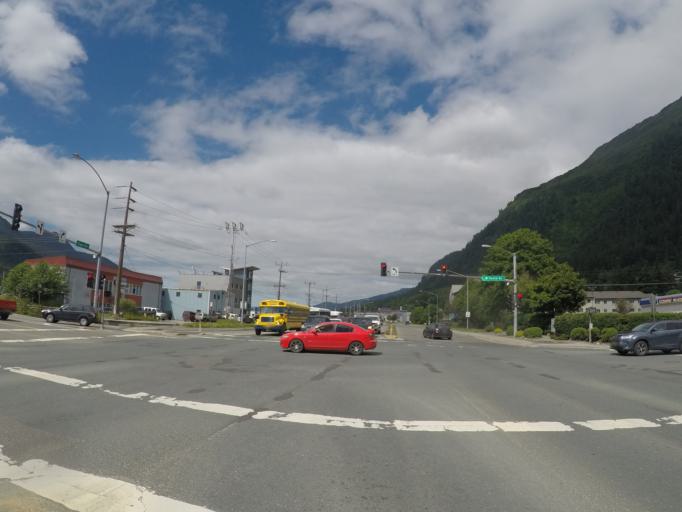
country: US
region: Alaska
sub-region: Juneau City and Borough
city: Juneau
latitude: 58.3010
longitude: -134.4244
